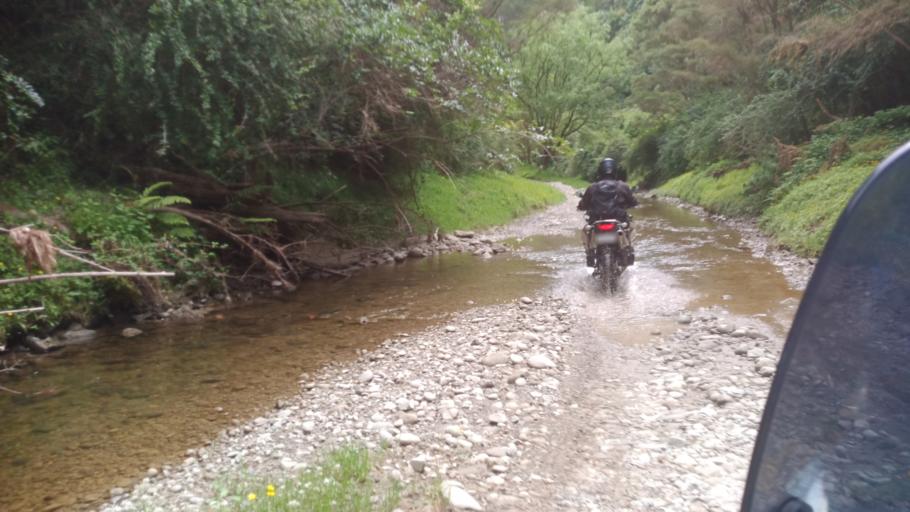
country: NZ
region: Gisborne
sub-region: Gisborne District
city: Gisborne
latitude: -38.4559
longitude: 177.9254
